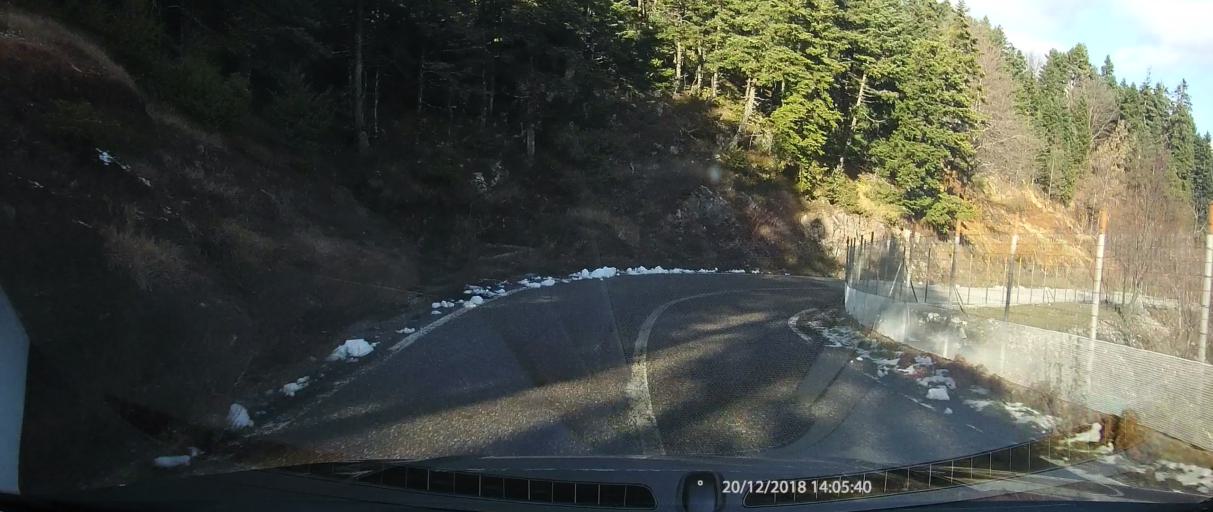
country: GR
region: West Greece
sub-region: Nomos Aitolias kai Akarnanias
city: Thermo
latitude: 38.7475
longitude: 21.6386
